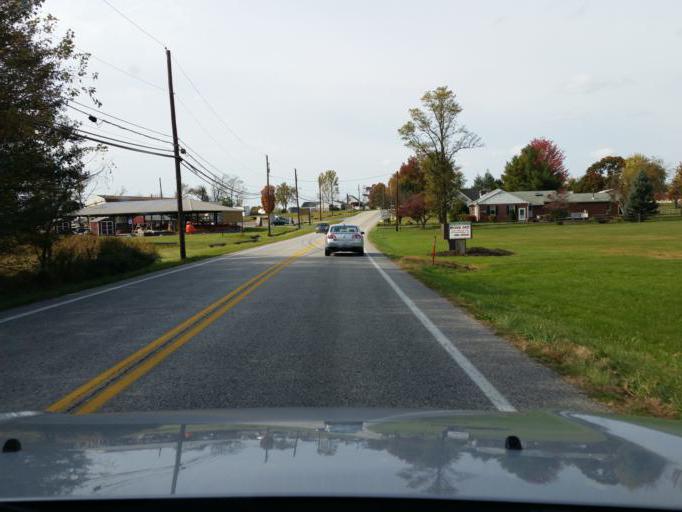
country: US
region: Pennsylvania
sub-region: Dauphin County
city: Skyline View
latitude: 40.3216
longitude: -76.7065
